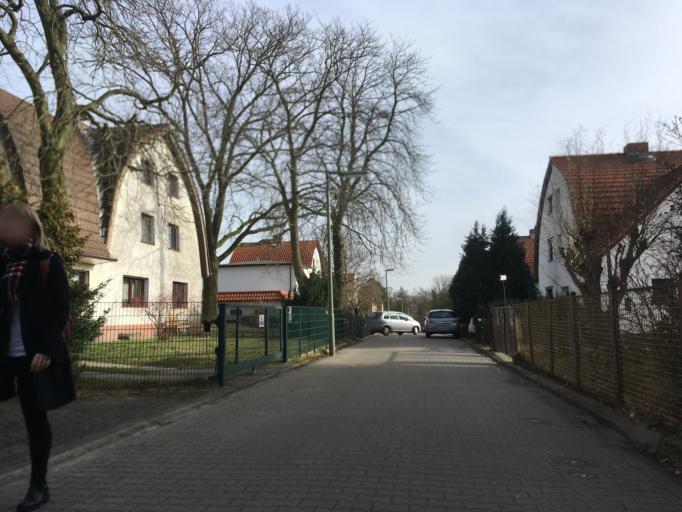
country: DE
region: Berlin
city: Lubars
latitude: 52.6138
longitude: 13.3482
